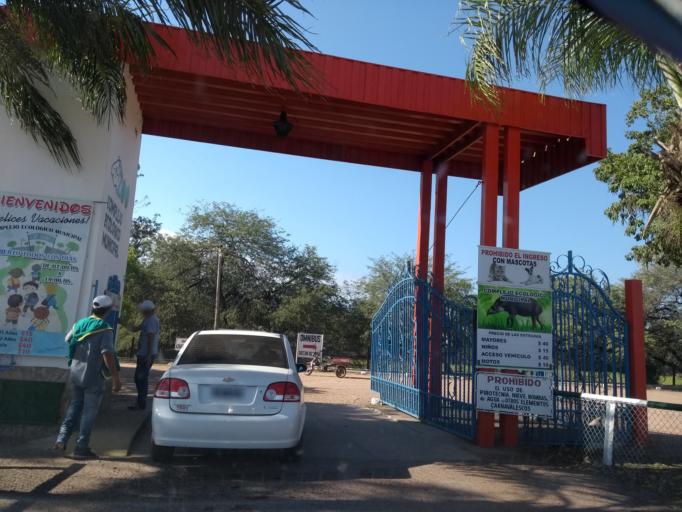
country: AR
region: Chaco
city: Presidencia Roque Saenz Pena
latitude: -26.8173
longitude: -60.4202
